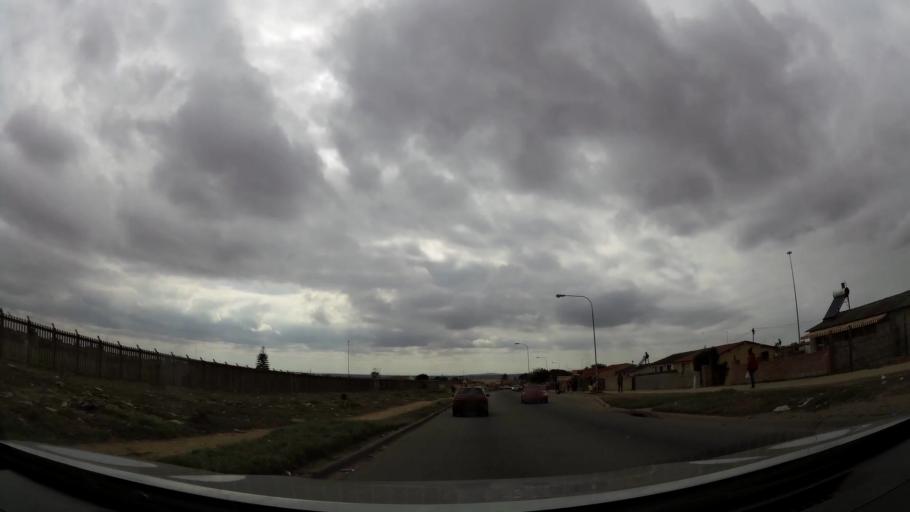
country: ZA
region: Eastern Cape
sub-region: Nelson Mandela Bay Metropolitan Municipality
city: Port Elizabeth
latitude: -33.8750
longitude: 25.5624
